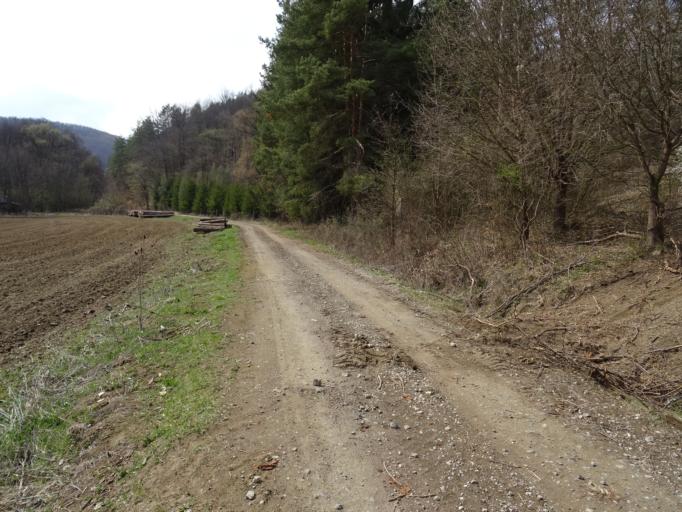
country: HU
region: Nograd
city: Matranovak
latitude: 48.0856
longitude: 20.0004
